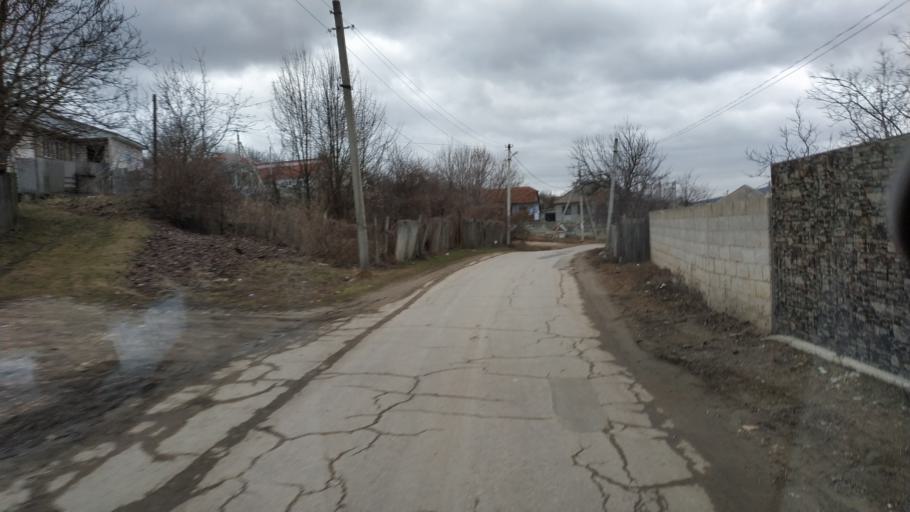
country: MD
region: Calarasi
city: Calarasi
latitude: 47.2421
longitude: 28.3084
